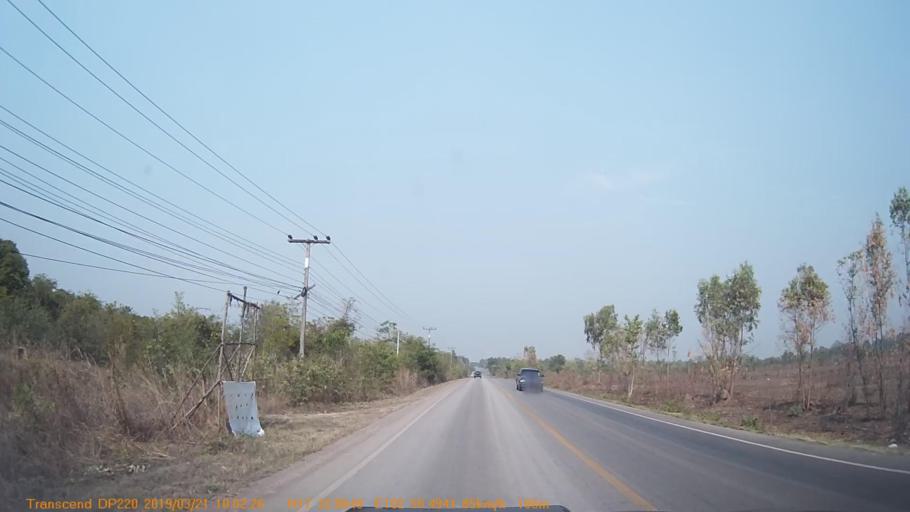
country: TH
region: Changwat Udon Thani
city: Udon Thani
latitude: 17.5478
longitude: 102.8413
